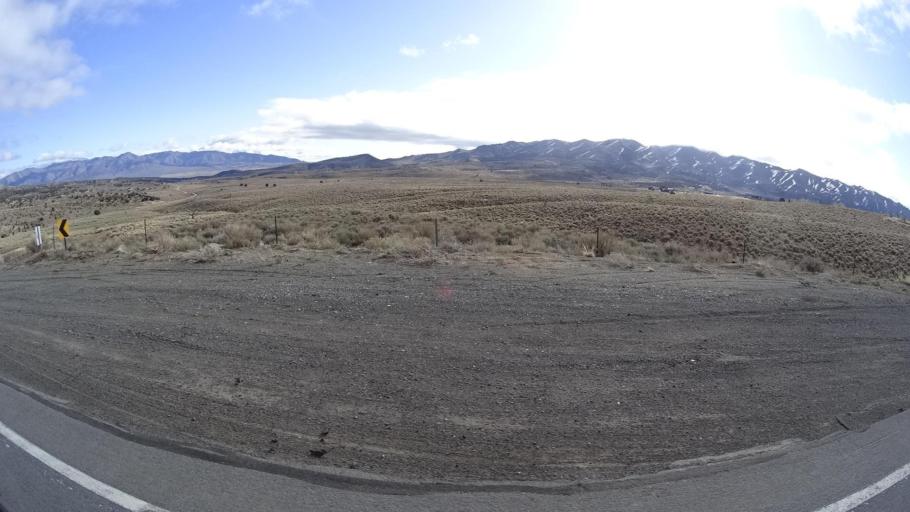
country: US
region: Nevada
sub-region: Washoe County
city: Cold Springs
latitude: 39.7974
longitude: -119.9010
